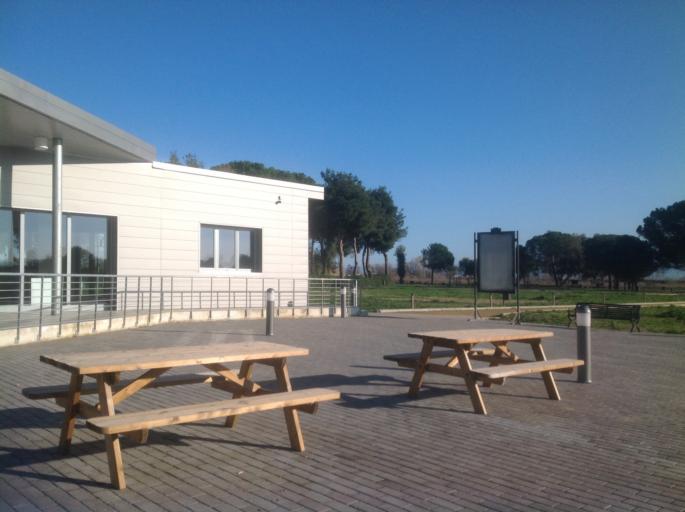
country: IT
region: Calabria
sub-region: Provincia di Cosenza
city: Sibari
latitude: 39.7176
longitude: 16.4910
